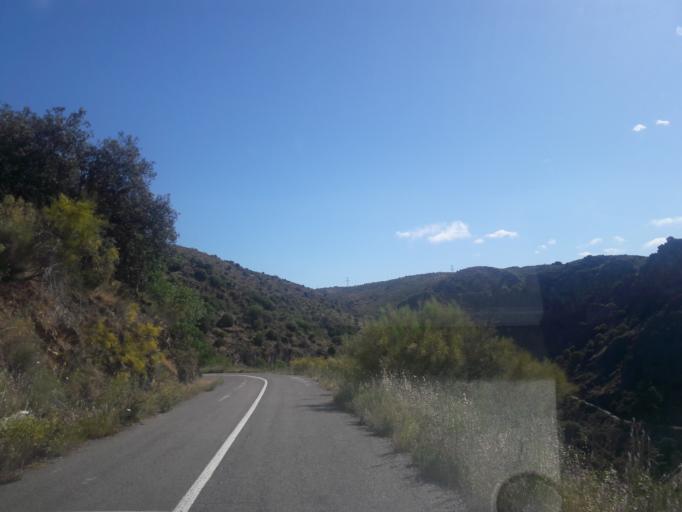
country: ES
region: Castille and Leon
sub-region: Provincia de Salamanca
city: Saucelle
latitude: 41.0349
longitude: -6.7453
